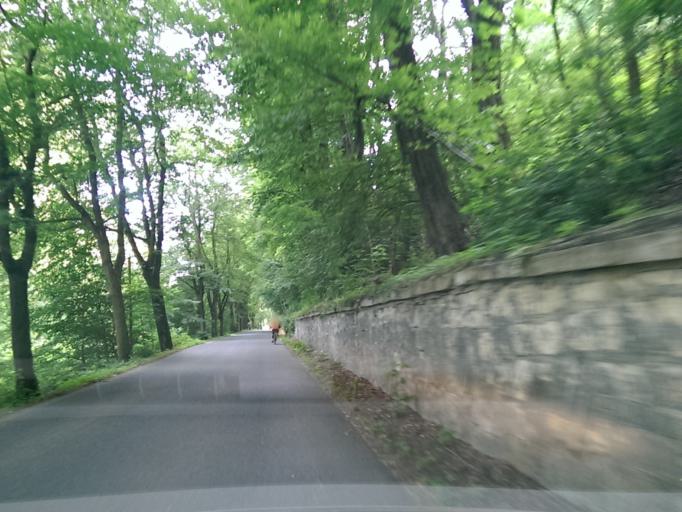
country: CZ
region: Central Bohemia
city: Kosmonosy
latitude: 50.4649
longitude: 14.9144
